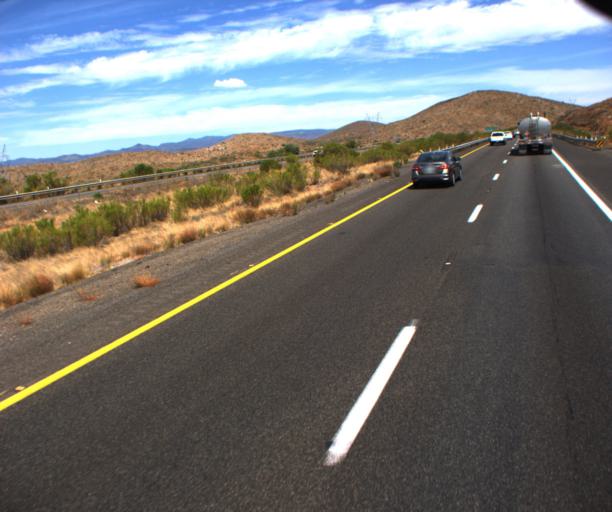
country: US
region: Arizona
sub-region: Yavapai County
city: Cordes Lakes
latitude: 34.2829
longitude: -112.1196
